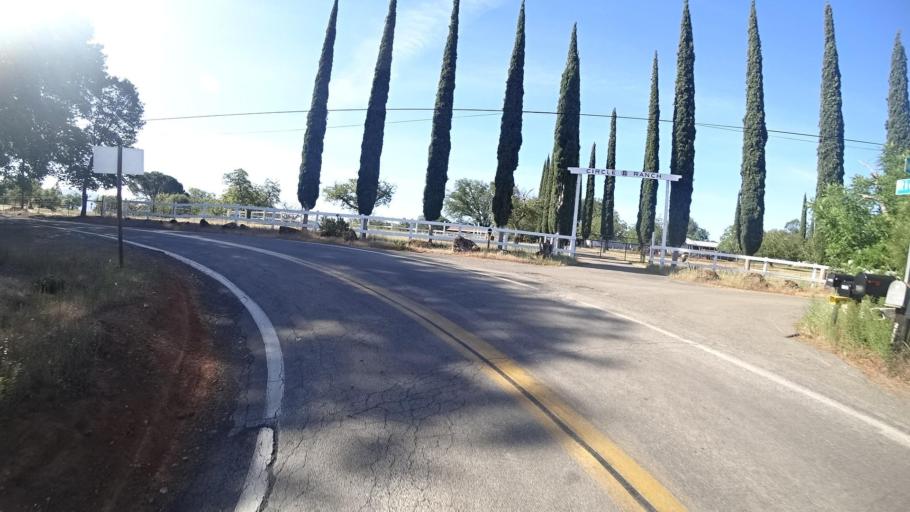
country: US
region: California
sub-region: Lake County
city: Lakeport
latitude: 39.0442
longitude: -122.9520
